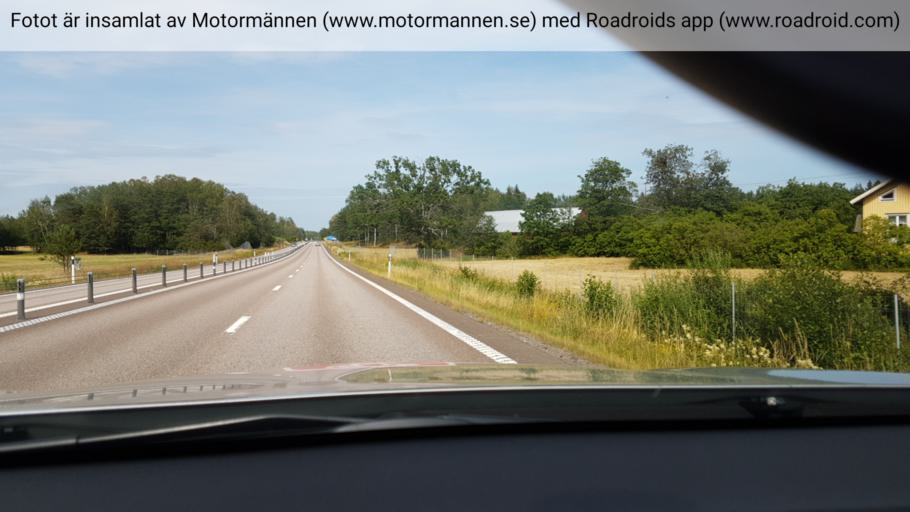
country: SE
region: Vaestra Goetaland
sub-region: Melleruds Kommun
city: Mellerud
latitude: 58.8364
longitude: 12.5393
